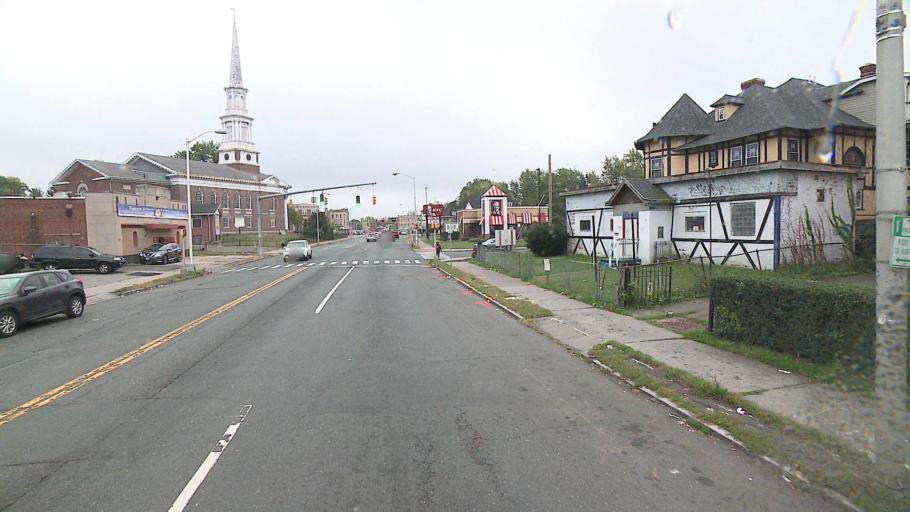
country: US
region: Connecticut
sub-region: Hartford County
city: Hartford
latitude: 41.7799
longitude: -72.6904
